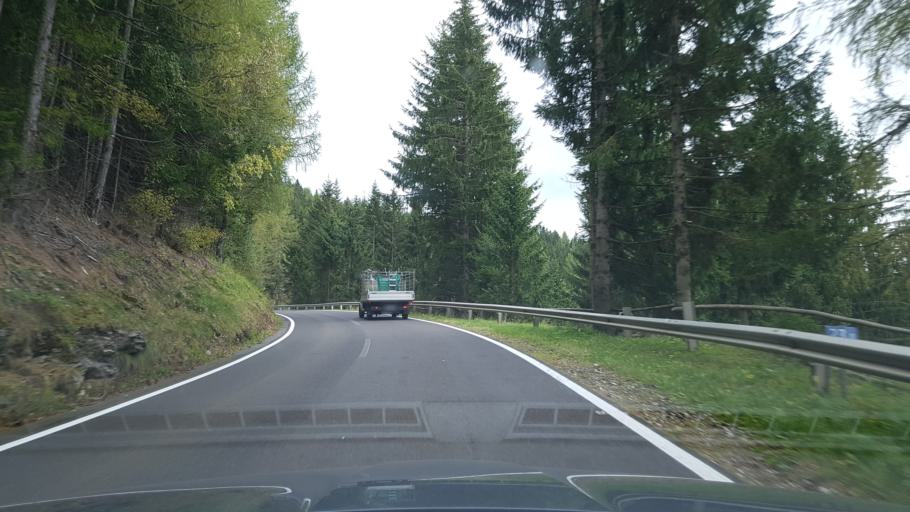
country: AT
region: Styria
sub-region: Politischer Bezirk Murtal
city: Kleinlobming
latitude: 47.1255
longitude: 14.8862
